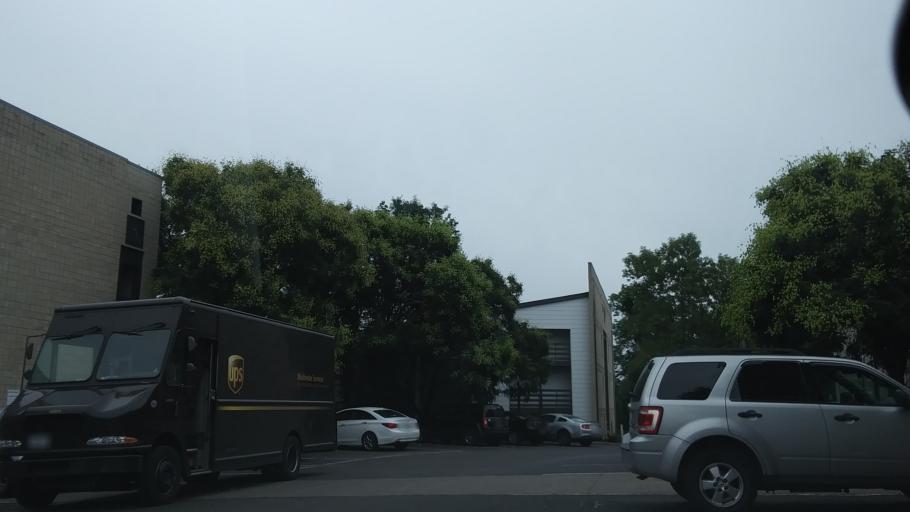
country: US
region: Tennessee
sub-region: Davidson County
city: Belle Meade
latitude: 36.1457
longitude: -86.8551
